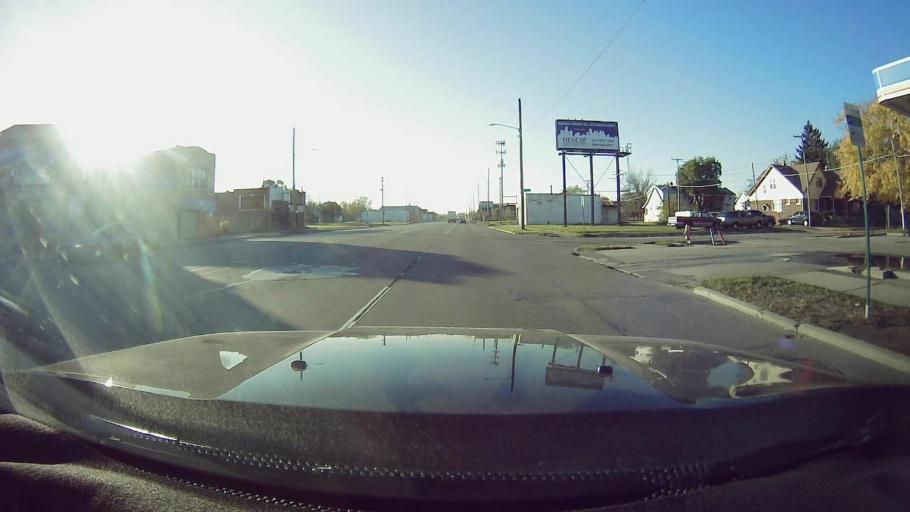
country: US
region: Michigan
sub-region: Wayne County
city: Hamtramck
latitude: 42.3987
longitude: -83.0230
